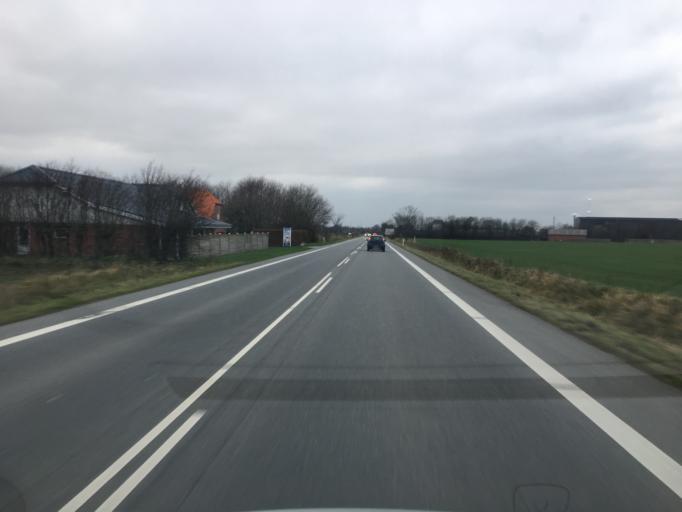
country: DK
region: South Denmark
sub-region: Aabenraa Kommune
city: Rodekro
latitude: 55.0268
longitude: 9.3277
